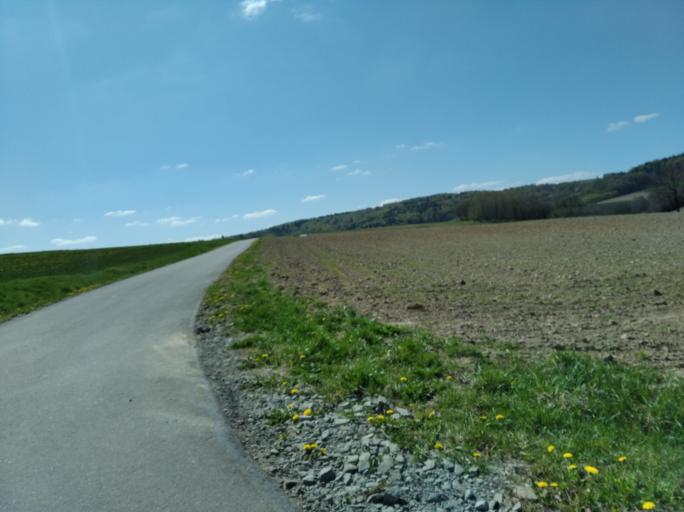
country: PL
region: Subcarpathian Voivodeship
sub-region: Powiat strzyzowski
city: Wisniowa
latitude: 49.9086
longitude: 21.6870
